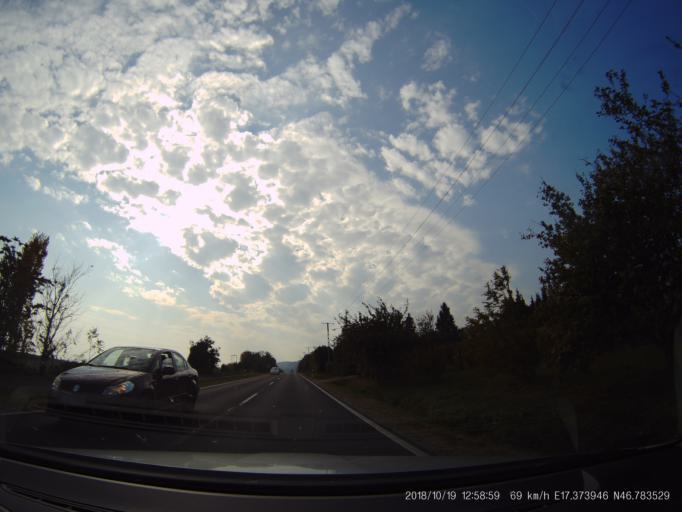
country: HU
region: Zala
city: Vonyarcvashegy
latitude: 46.7835
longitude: 17.3739
